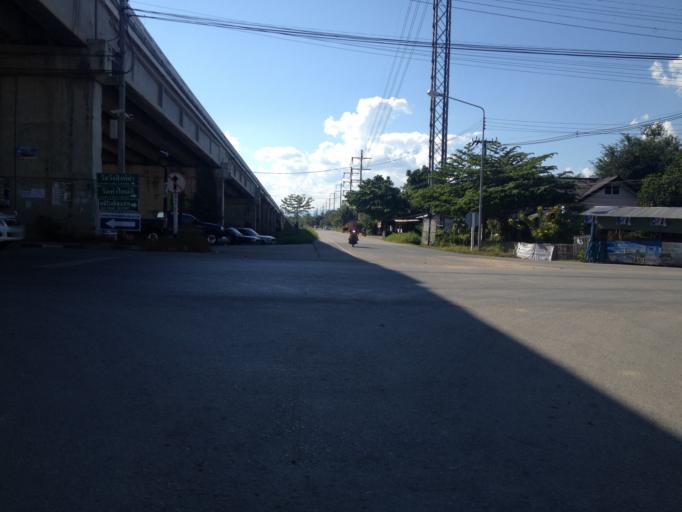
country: TH
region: Chiang Mai
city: Saraphi
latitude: 18.7200
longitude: 98.9863
